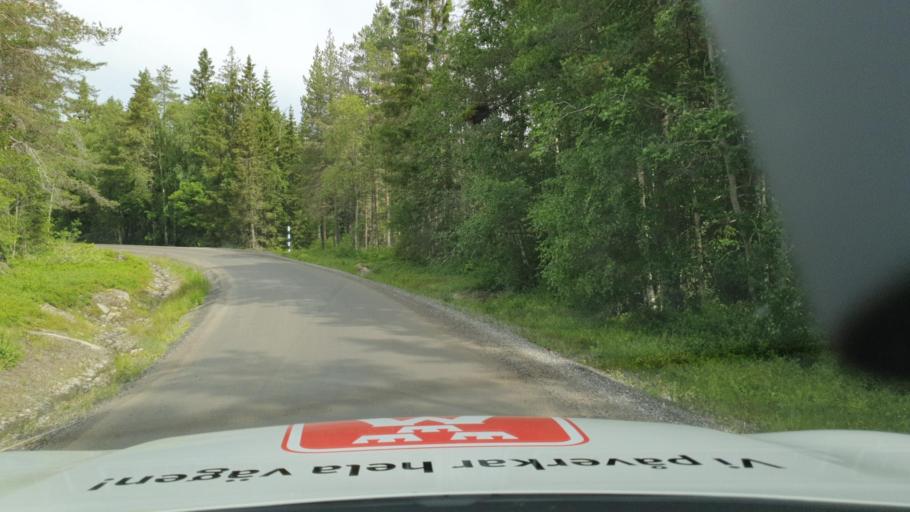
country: SE
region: Vaesterbotten
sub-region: Robertsfors Kommun
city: Robertsfors
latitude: 64.0273
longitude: 20.8881
